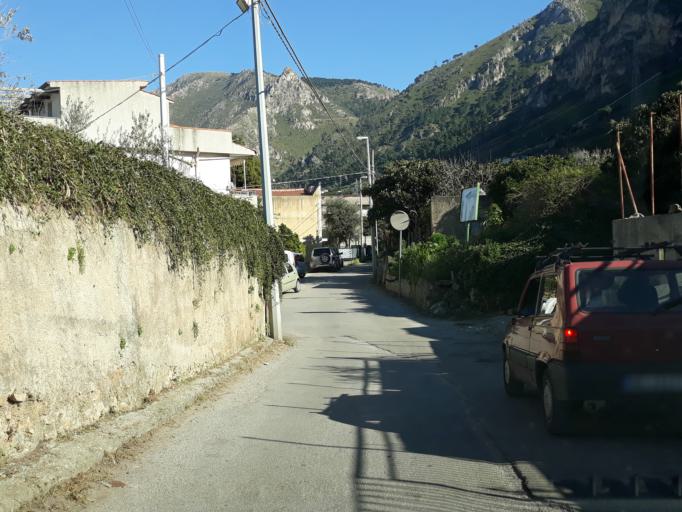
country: IT
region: Sicily
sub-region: Palermo
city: Villa Ciambra
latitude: 38.0755
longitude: 13.3529
